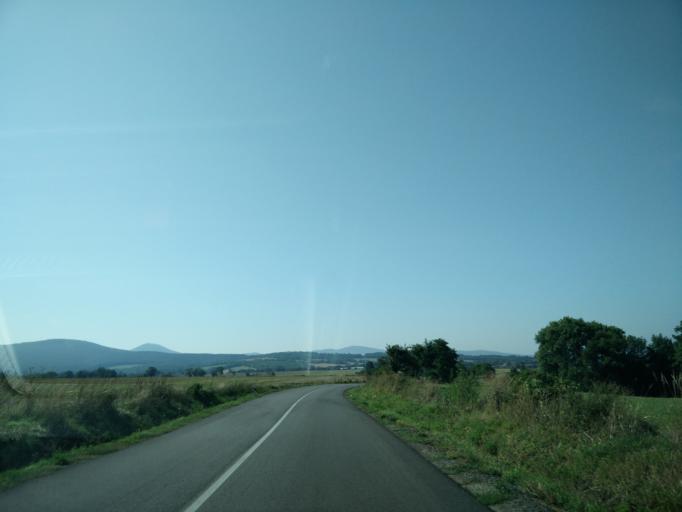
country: SK
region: Nitriansky
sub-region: Okres Nitra
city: Nitra
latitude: 48.4383
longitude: 18.1351
